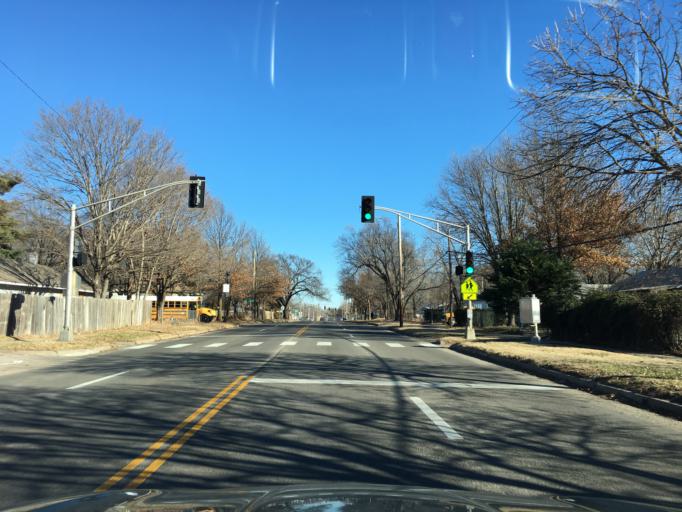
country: US
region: Kansas
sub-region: Sedgwick County
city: Wichita
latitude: 37.6719
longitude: -97.2837
